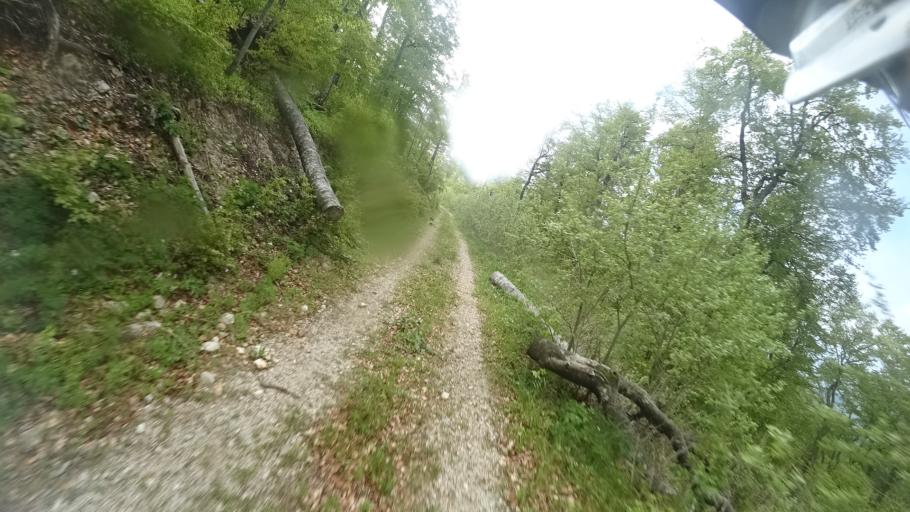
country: BA
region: Federation of Bosnia and Herzegovina
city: Orasac
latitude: 44.5737
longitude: 15.8721
